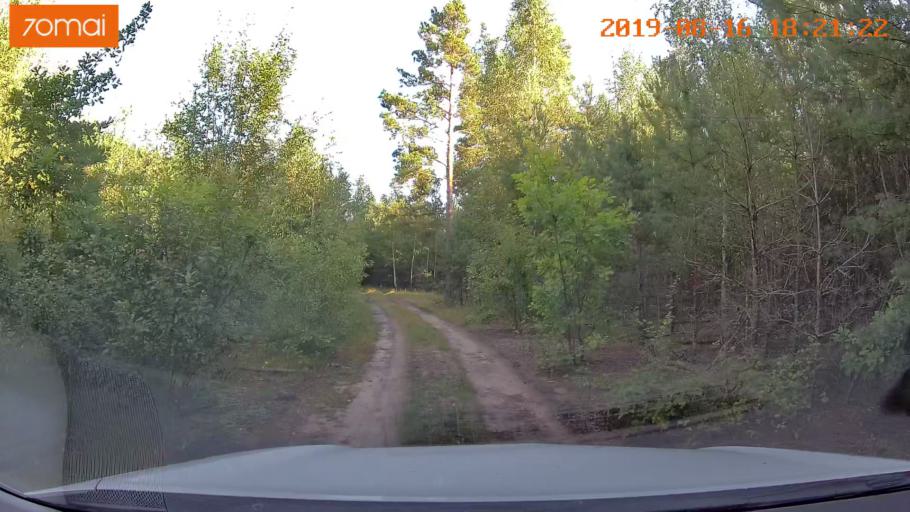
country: BY
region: Mogilev
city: Asipovichy
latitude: 53.2064
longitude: 28.6338
